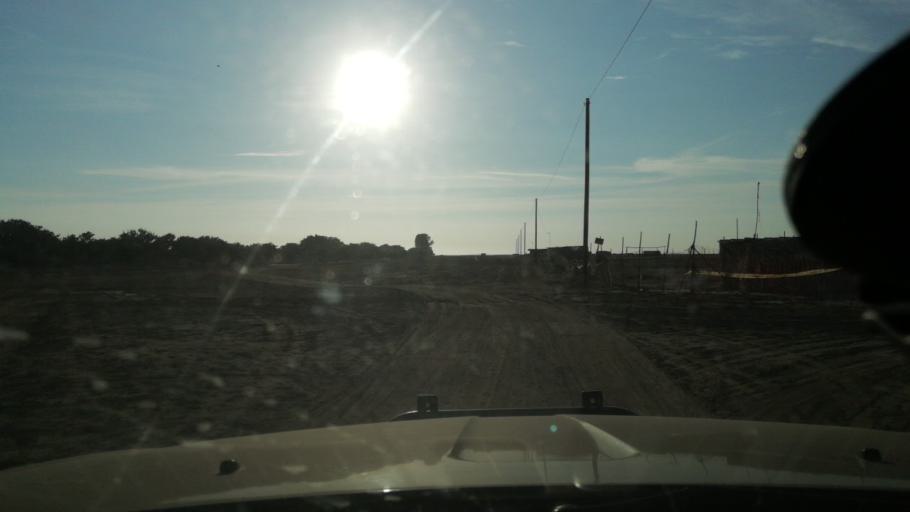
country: PE
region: Ica
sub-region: Provincia de Chincha
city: San Pedro
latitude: -13.3315
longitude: -76.1802
